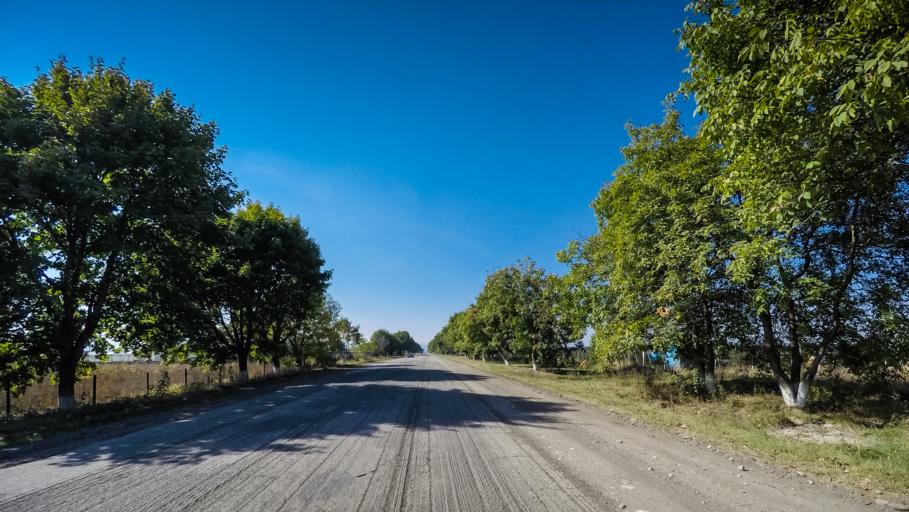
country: RU
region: Kabardino-Balkariya
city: Chegem Vtoroy
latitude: 43.5780
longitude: 43.5740
